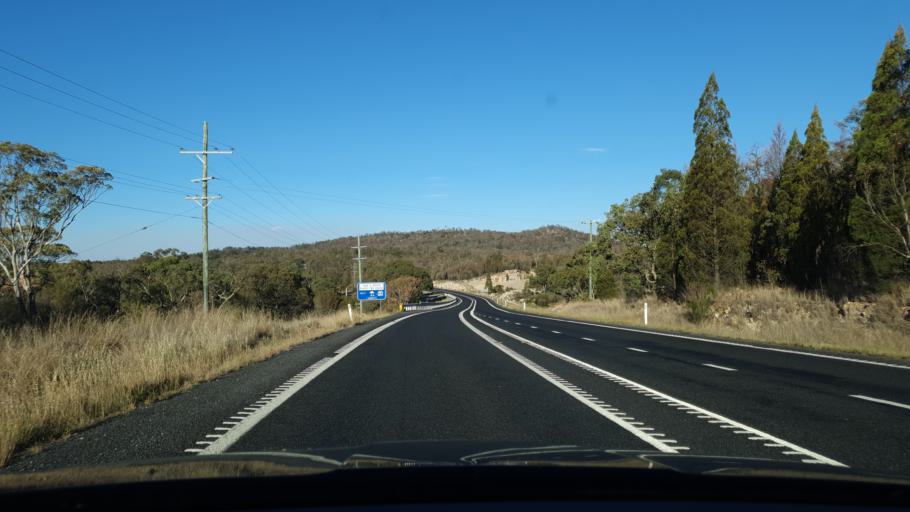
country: AU
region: Queensland
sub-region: Southern Downs
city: Stanthorpe
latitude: -28.6849
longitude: 151.9143
